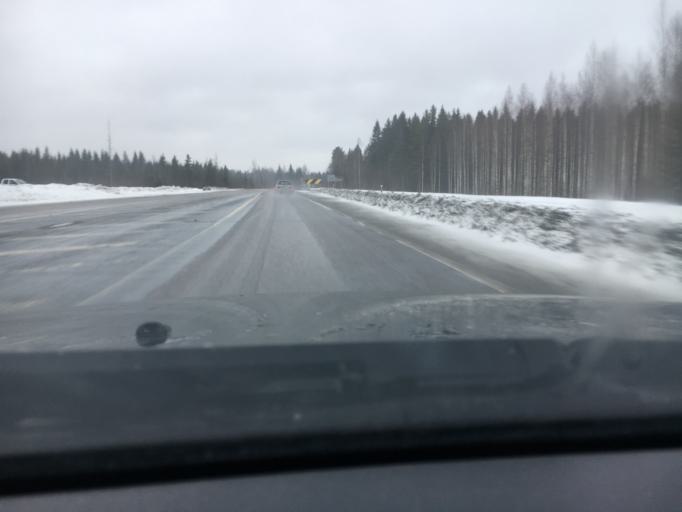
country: FI
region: Central Finland
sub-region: Joutsa
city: Joutsa
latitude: 61.7788
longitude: 26.0969
